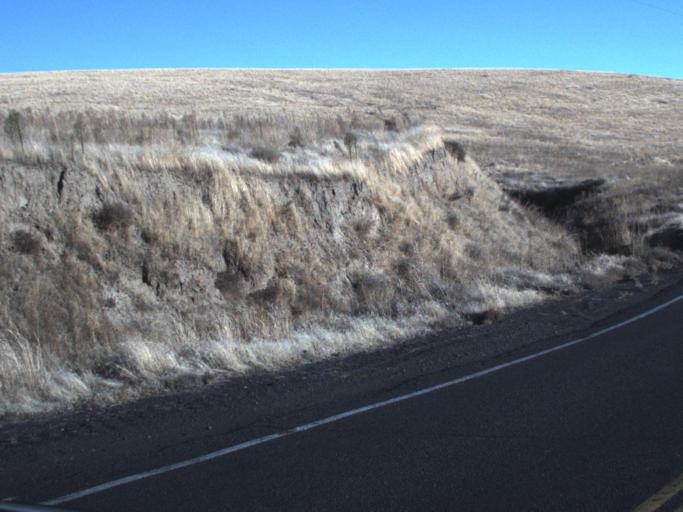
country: US
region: Washington
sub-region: Adams County
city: Ritzville
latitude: 46.6860
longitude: -118.3861
